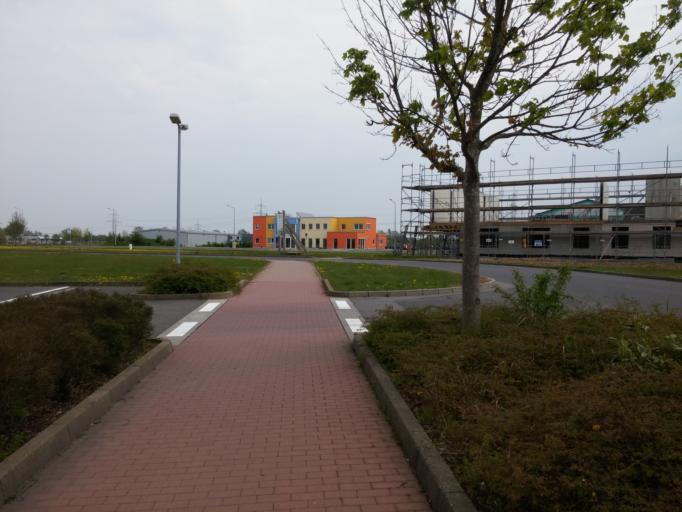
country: DE
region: Mecklenburg-Vorpommern
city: Roggentin
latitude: 54.0756
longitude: 12.2042
